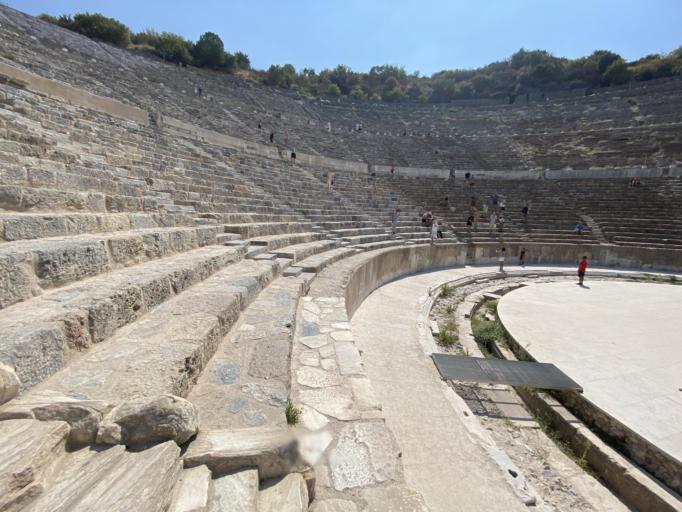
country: TR
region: Izmir
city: Selcuk
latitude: 37.9412
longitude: 27.3424
